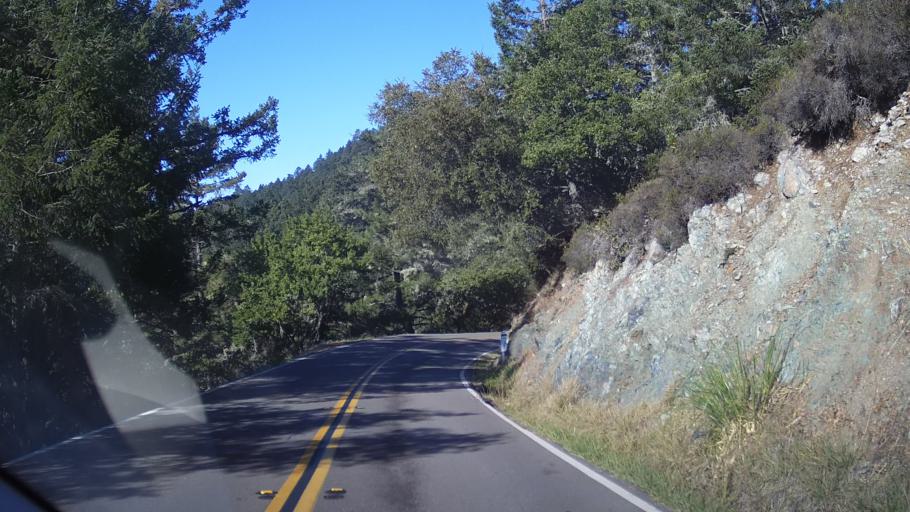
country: US
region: California
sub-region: Marin County
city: Mill Valley
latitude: 37.9036
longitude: -122.6060
